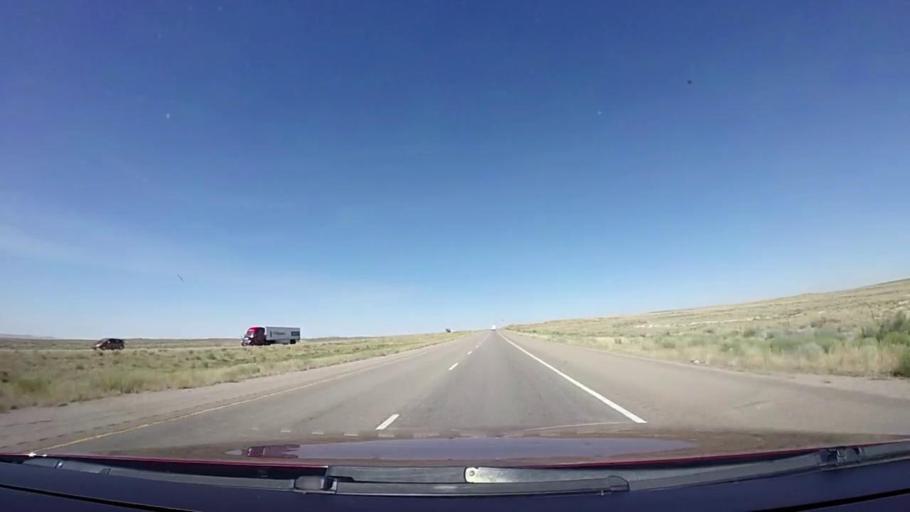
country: US
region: Wyoming
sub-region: Sweetwater County
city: Rock Springs
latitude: 41.6388
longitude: -108.4620
